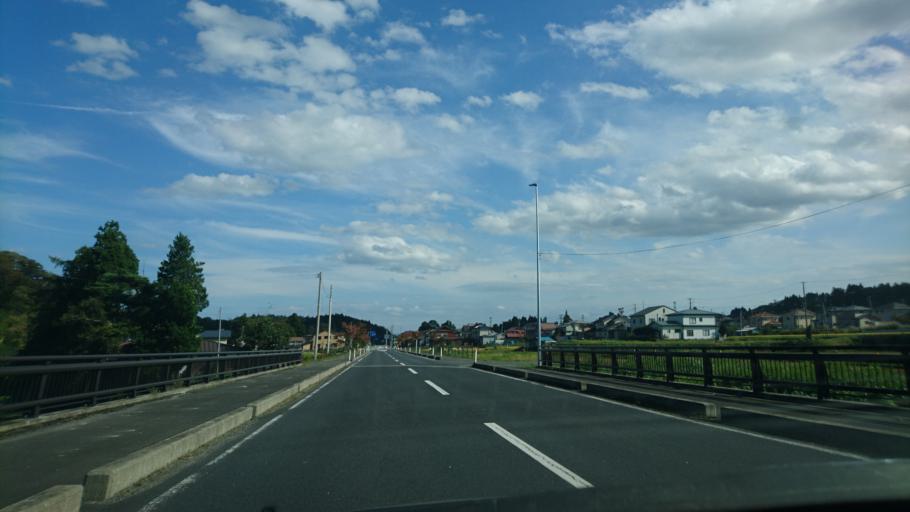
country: JP
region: Iwate
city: Ichinoseki
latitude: 38.8697
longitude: 141.1187
